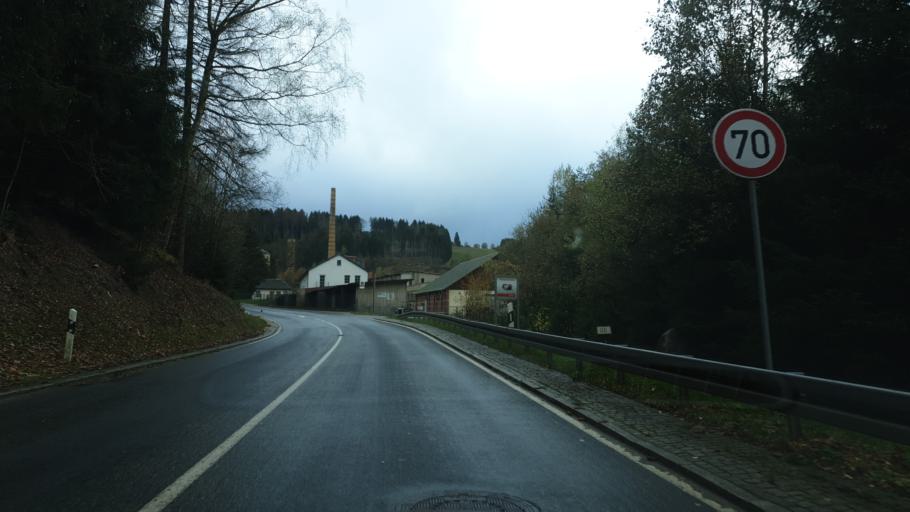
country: DE
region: Saxony
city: Schoenheide
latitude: 50.4958
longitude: 12.5483
